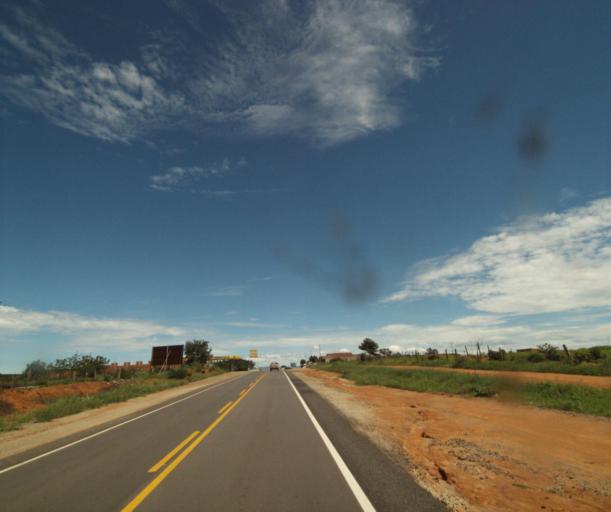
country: BR
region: Bahia
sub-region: Guanambi
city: Guanambi
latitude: -14.3814
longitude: -42.7685
